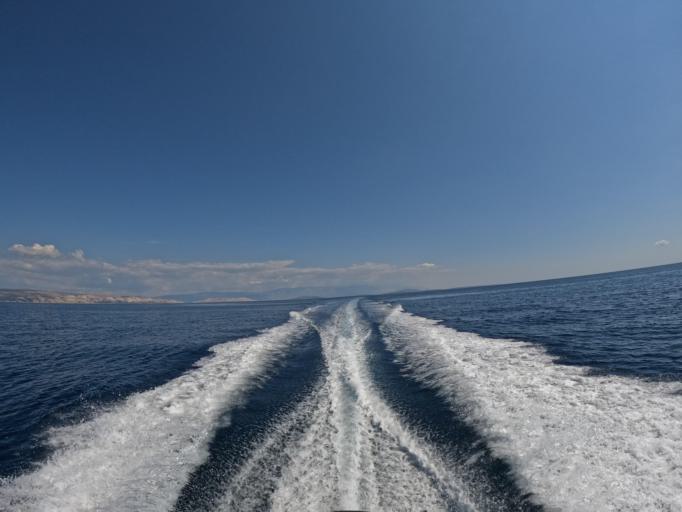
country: HR
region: Primorsko-Goranska
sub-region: Grad Krk
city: Krk
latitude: 44.9324
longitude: 14.5189
